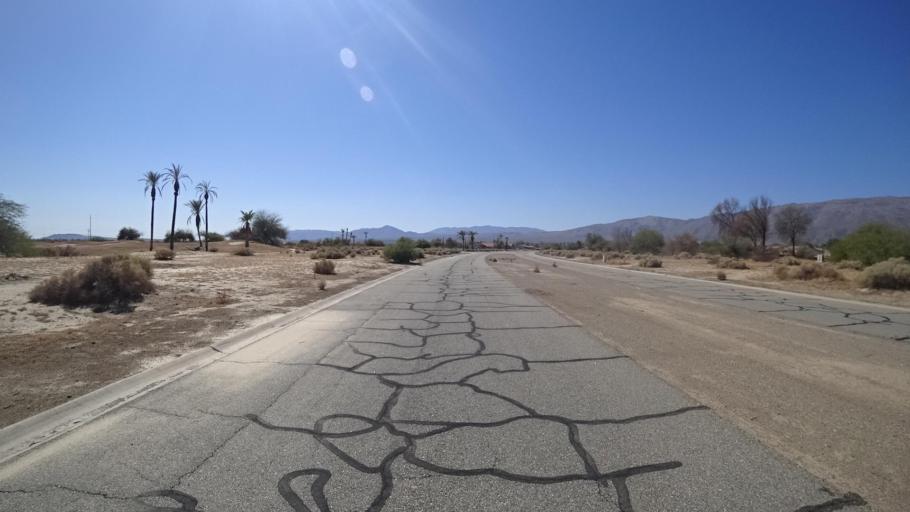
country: US
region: California
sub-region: San Diego County
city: Borrego Springs
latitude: 33.2451
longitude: -116.3515
